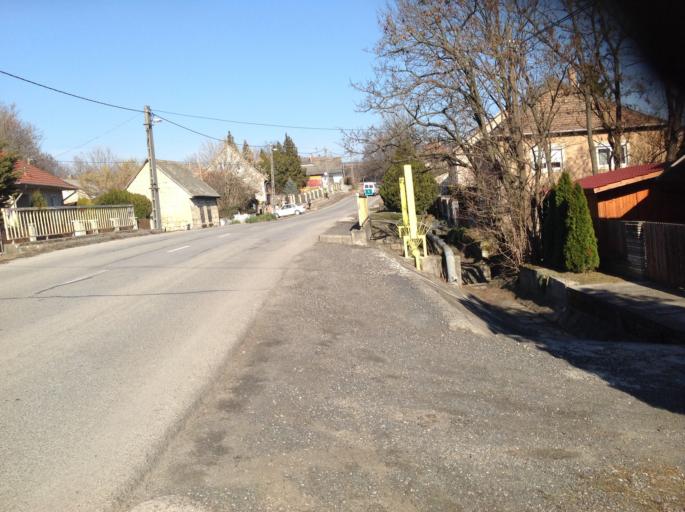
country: HU
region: Pest
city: Soskut
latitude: 47.4058
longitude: 18.8225
